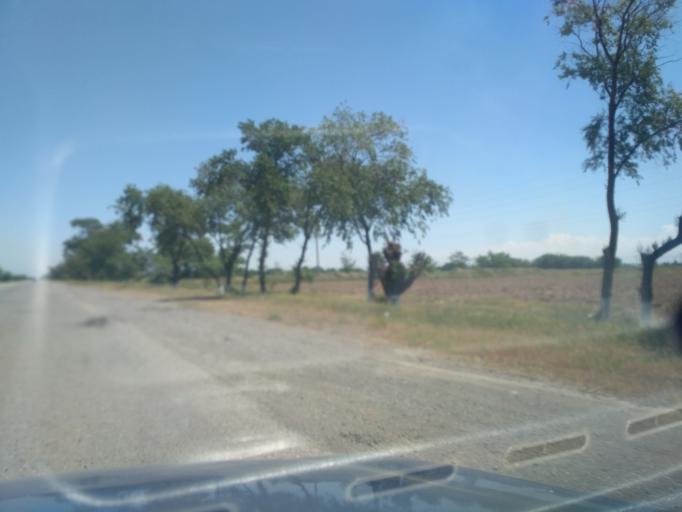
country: TJ
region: Viloyati Sughd
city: Zafarobod
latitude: 40.2190
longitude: 68.9052
